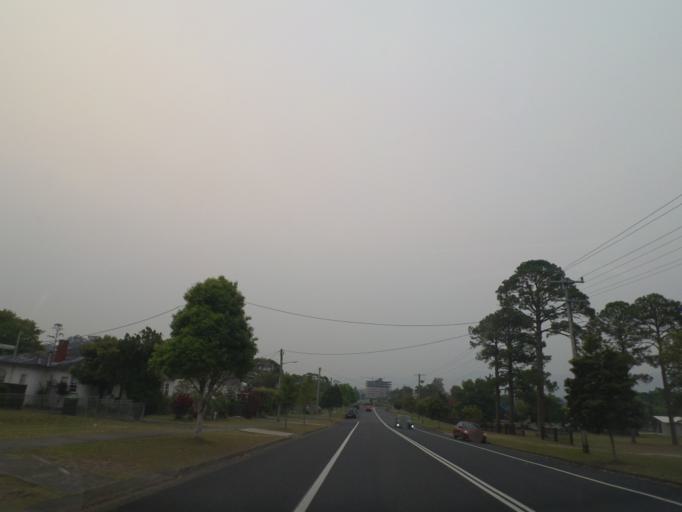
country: AU
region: New South Wales
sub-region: Coffs Harbour
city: Coffs Harbour
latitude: -30.3021
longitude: 153.1177
